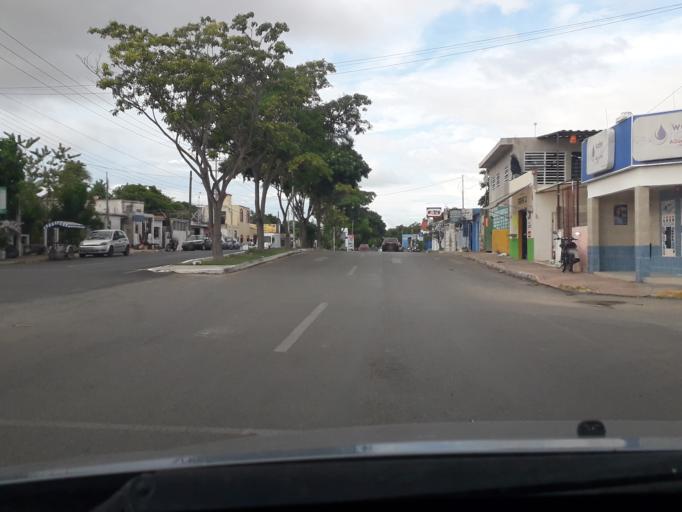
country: MX
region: Yucatan
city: Merida
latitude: 20.9664
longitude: -89.6636
